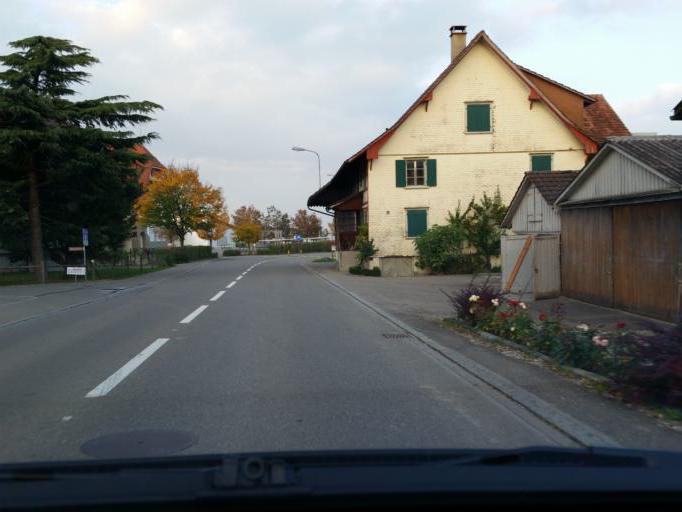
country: CH
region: Thurgau
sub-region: Arbon District
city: Uttwil
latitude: 47.5768
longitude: 9.3212
